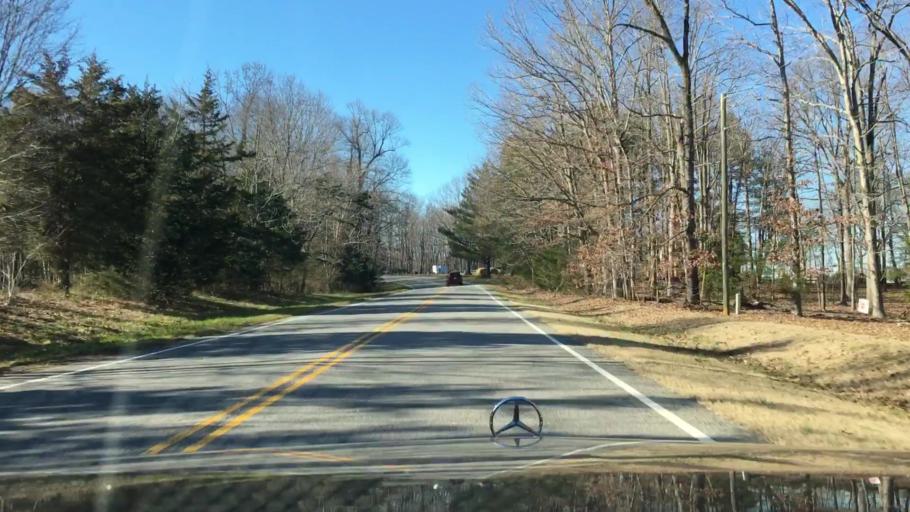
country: US
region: Virginia
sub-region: City of Bedford
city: Bedford
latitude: 37.2221
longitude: -79.5091
